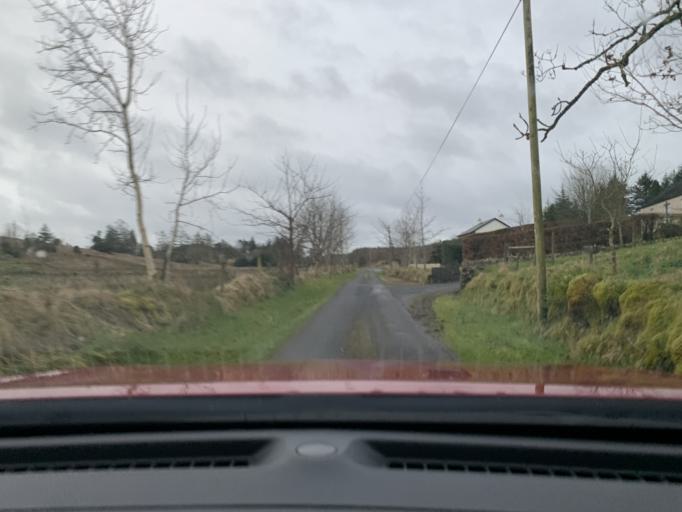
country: IE
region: Connaught
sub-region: Roscommon
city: Boyle
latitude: 54.0058
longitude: -8.3988
